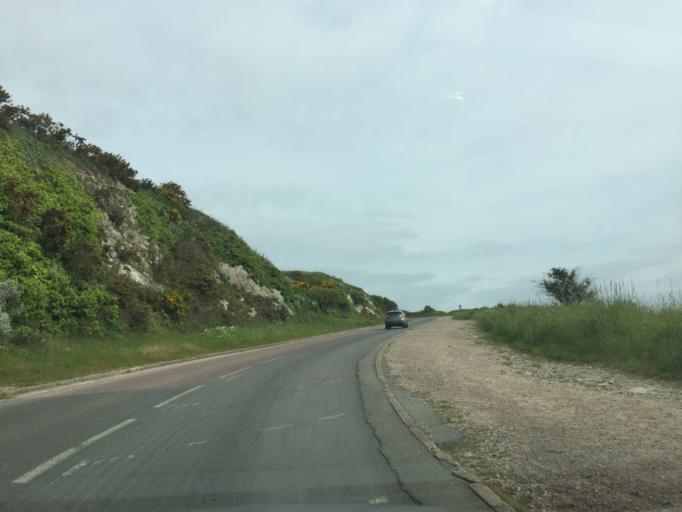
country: FR
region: Brittany
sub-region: Departement des Cotes-d'Armor
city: Saint-Cast-le-Guildo
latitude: 48.6423
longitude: -2.2456
